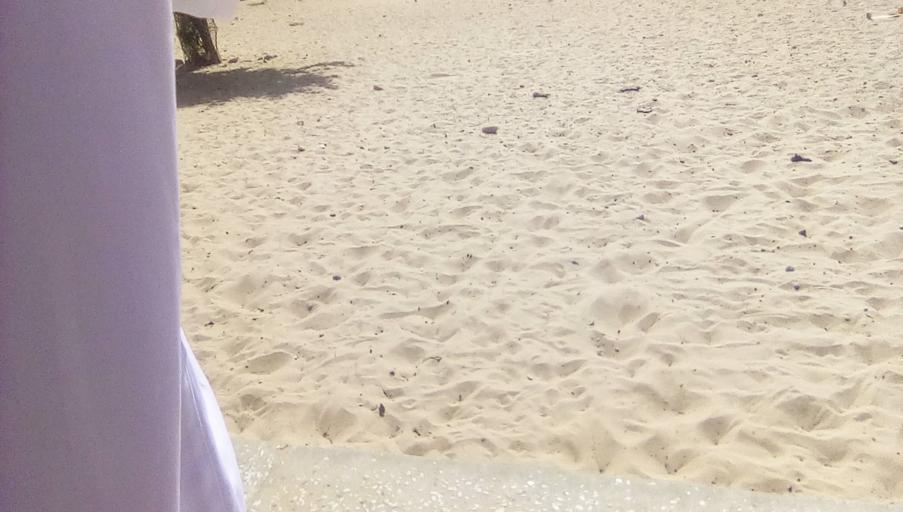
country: SN
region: Saint-Louis
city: Saint-Louis
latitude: 16.0676
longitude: -16.4213
